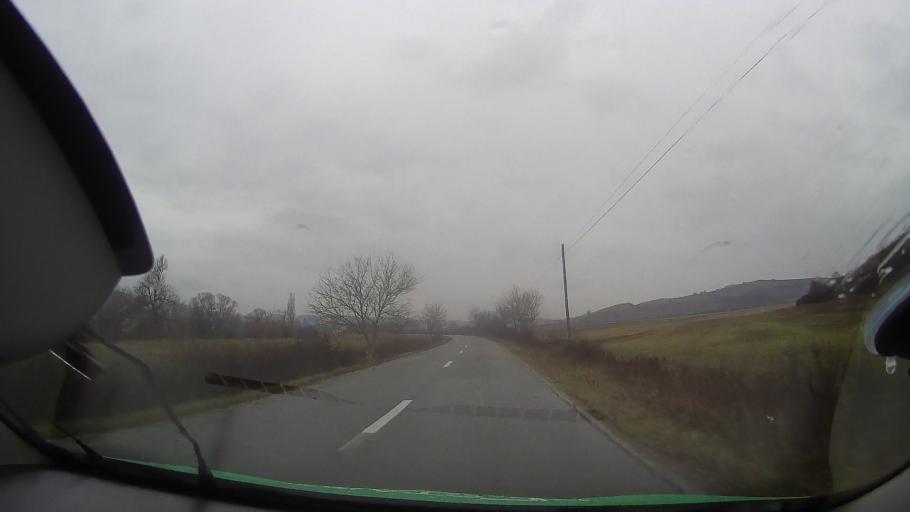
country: RO
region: Bihor
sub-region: Comuna Uileacu de Beius
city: Uileacu de Beius
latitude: 46.6810
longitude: 22.2500
